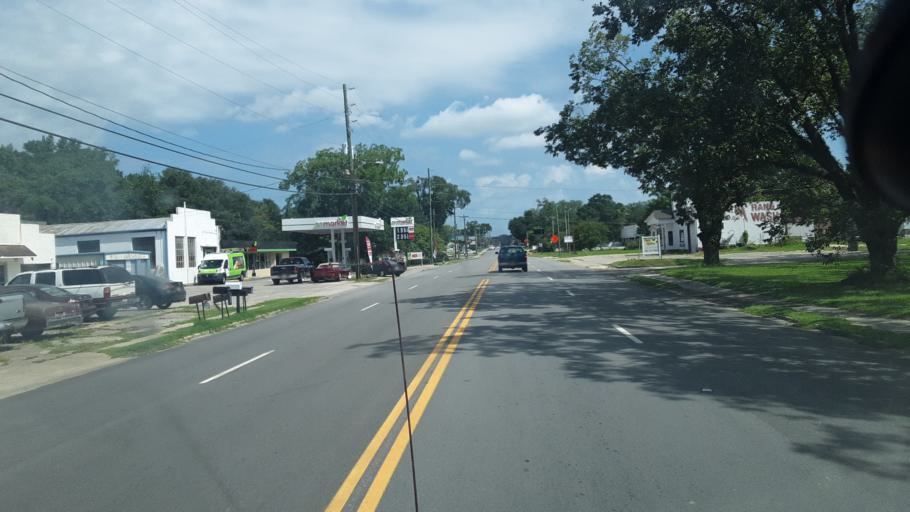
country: US
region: South Carolina
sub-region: Bamberg County
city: Bamberg
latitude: 33.2873
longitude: -81.0387
